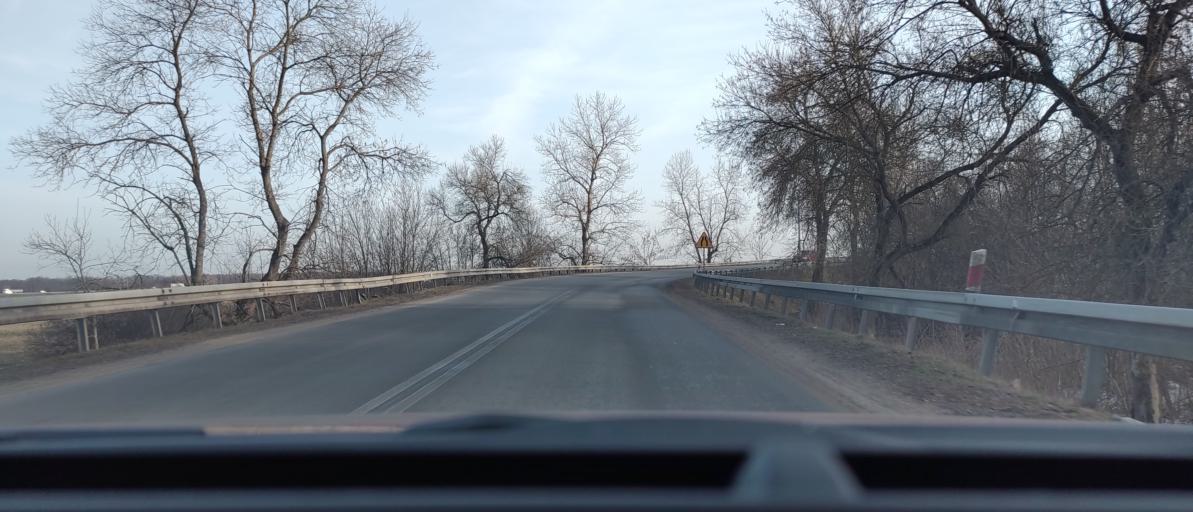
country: PL
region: Masovian Voivodeship
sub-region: Powiat bialobrzeski
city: Bialobrzegi
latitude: 51.6606
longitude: 20.9524
